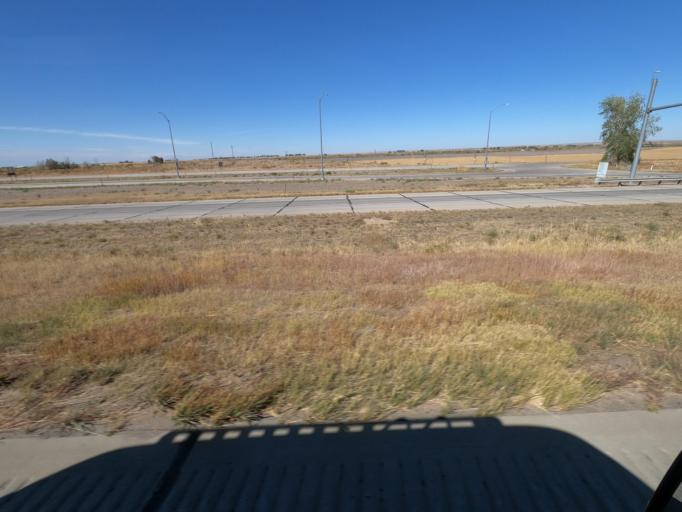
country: US
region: Colorado
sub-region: Morgan County
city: Fort Morgan
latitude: 40.2455
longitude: -103.8964
